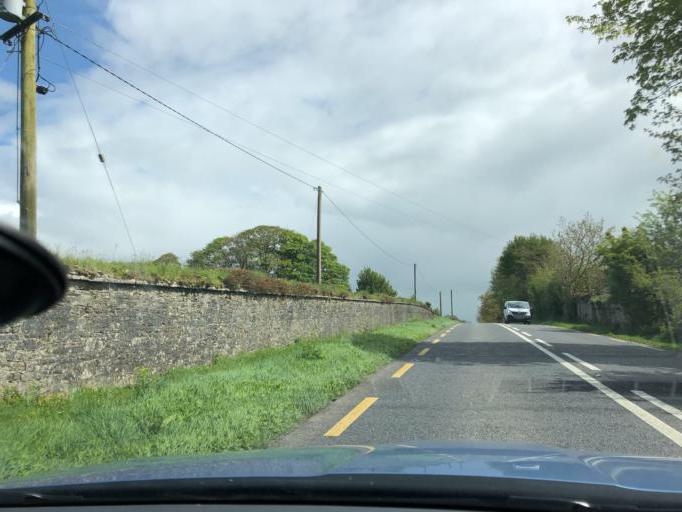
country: IE
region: Munster
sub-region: County Cork
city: Mitchelstown
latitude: 52.2649
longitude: -8.3008
